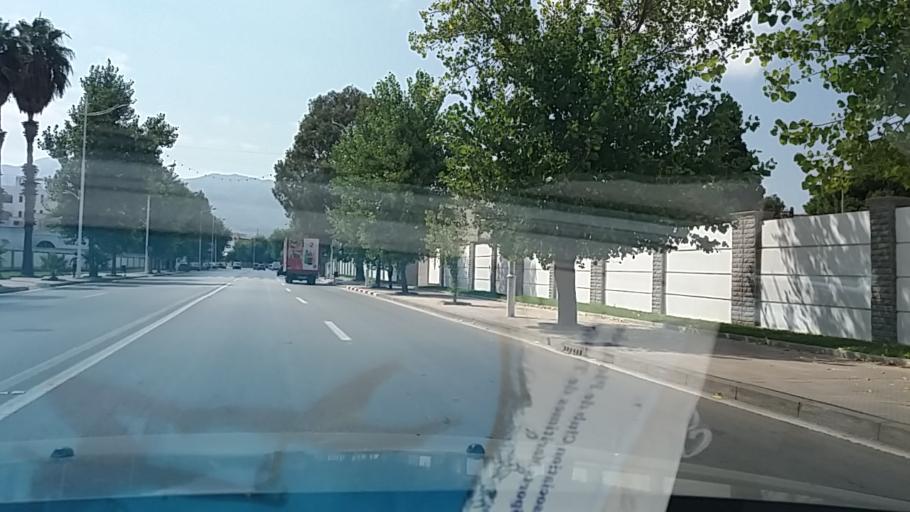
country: MA
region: Tanger-Tetouan
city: Tetouan
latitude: 35.5778
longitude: -5.3398
